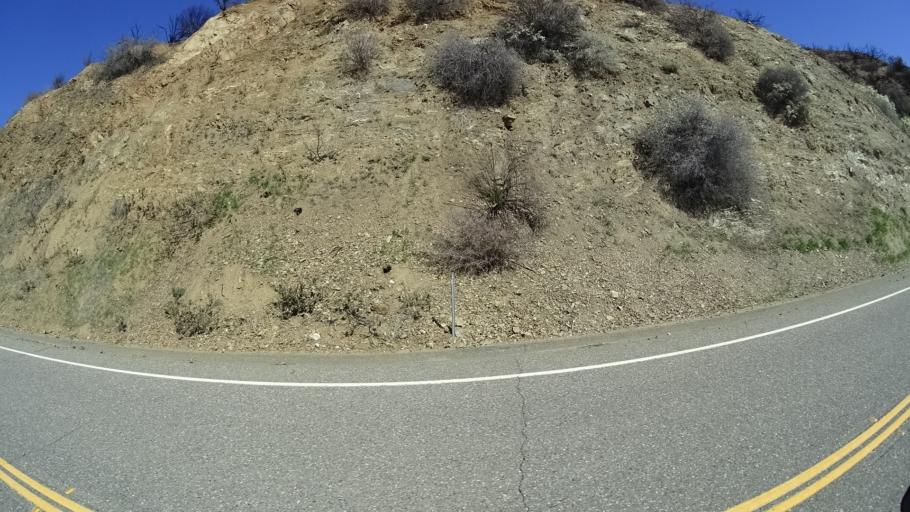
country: US
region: California
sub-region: Tehama County
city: Rancho Tehama Reserve
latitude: 39.6615
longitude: -122.6456
